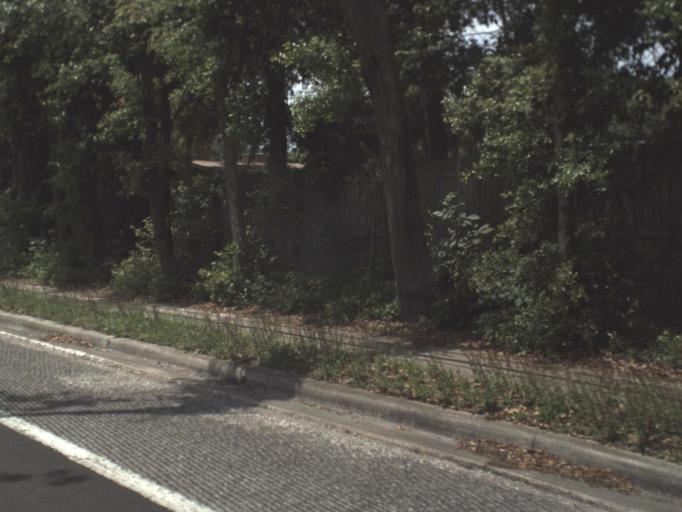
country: US
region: Florida
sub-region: Duval County
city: Jacksonville
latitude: 30.2343
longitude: -81.6189
